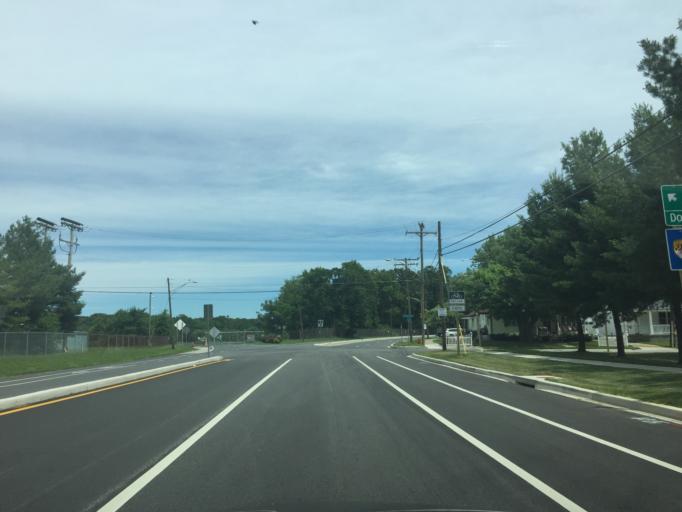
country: US
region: Maryland
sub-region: Baltimore County
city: Middle River
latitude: 39.3219
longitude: -76.4218
